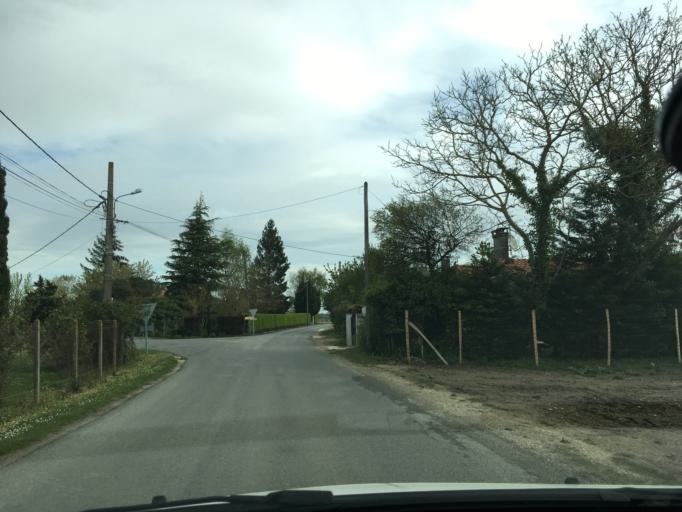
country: FR
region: Aquitaine
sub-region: Departement de la Gironde
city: Lesparre-Medoc
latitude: 45.3237
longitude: -0.8797
